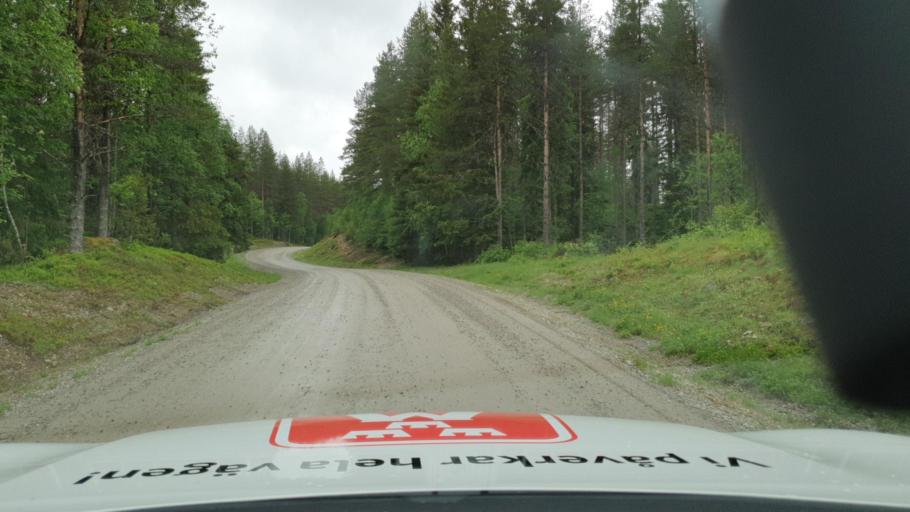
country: SE
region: Vaesterbotten
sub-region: Dorotea Kommun
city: Dorotea
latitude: 64.0311
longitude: 16.7678
